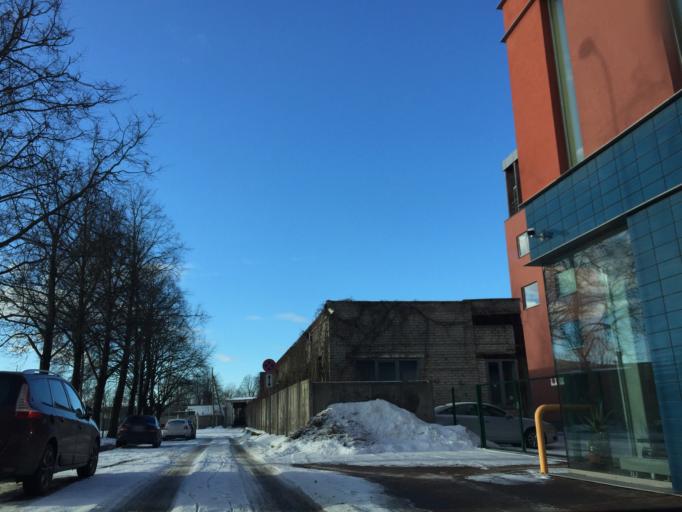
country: LV
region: Riga
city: Riga
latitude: 56.9365
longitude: 24.1463
